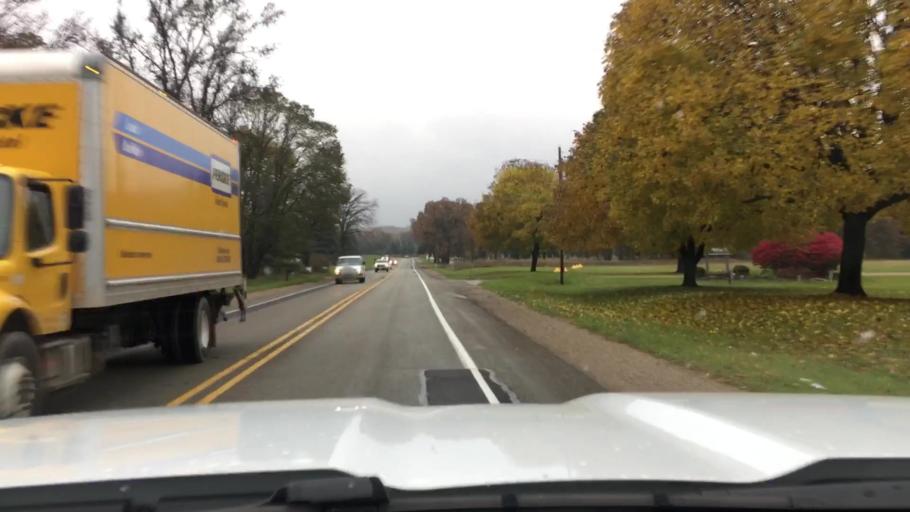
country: US
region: Michigan
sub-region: Kent County
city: Lowell
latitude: 42.9524
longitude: -85.3507
